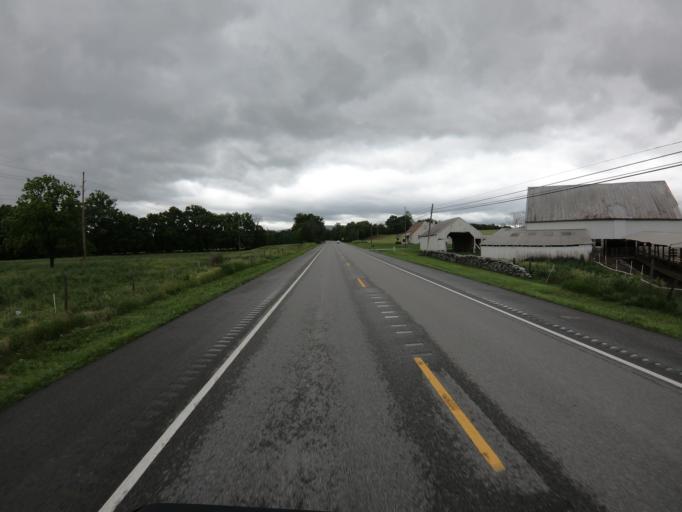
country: US
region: Maryland
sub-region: Washington County
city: Boonsboro
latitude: 39.4992
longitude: -77.6750
